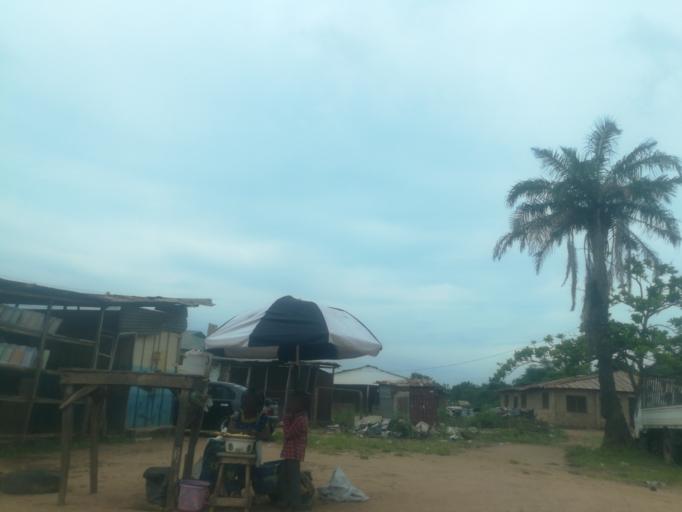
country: NG
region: Oyo
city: Ibadan
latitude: 7.3747
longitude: 3.9715
